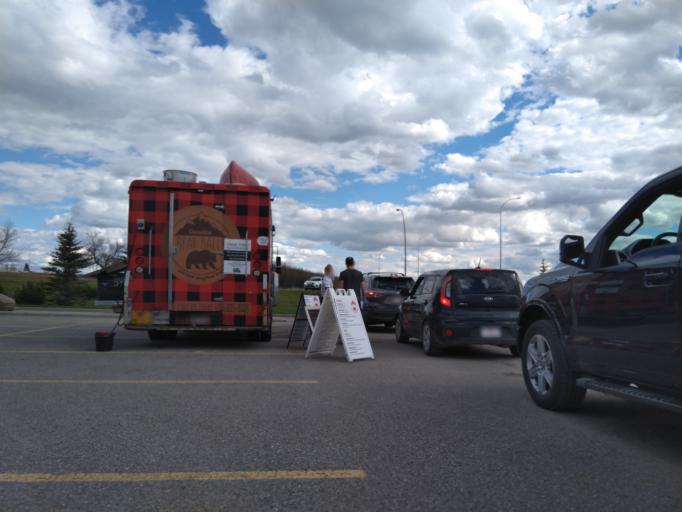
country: CA
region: Alberta
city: Calgary
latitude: 51.0066
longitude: -114.1453
